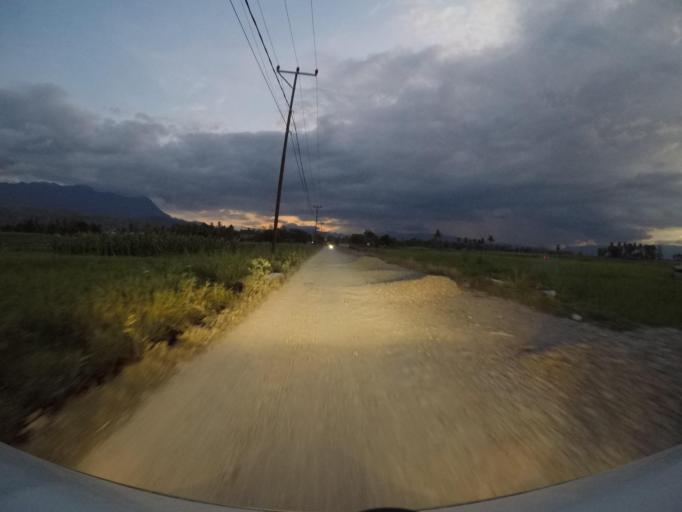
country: TL
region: Bobonaro
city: Maliana
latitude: -8.9848
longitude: 125.2108
